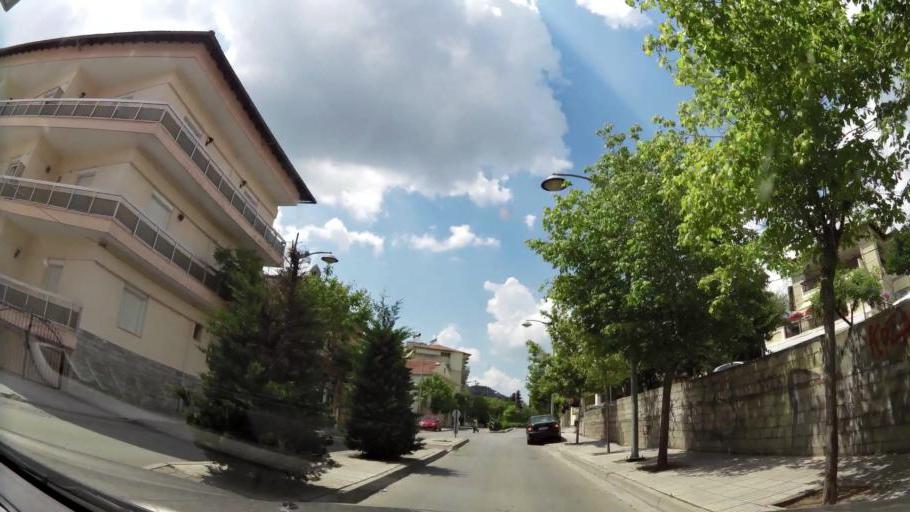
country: GR
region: West Macedonia
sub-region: Nomos Kozanis
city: Kozani
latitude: 40.3064
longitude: 21.7884
